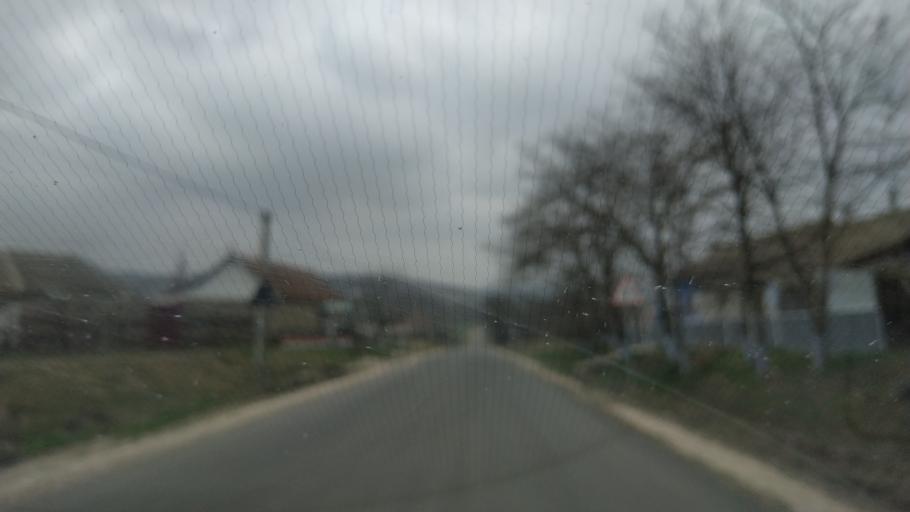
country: MD
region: Basarabeasca
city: Basarabeasca
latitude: 46.3572
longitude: 28.8232
